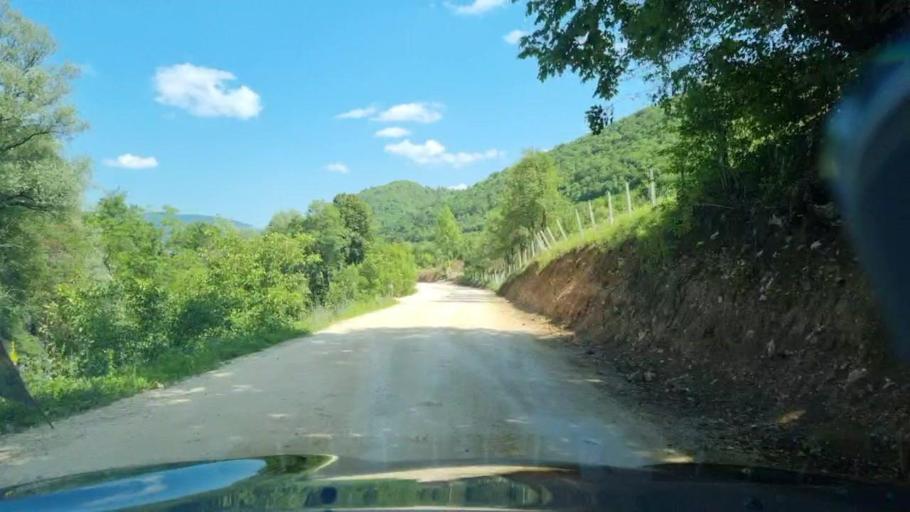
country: BA
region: Federation of Bosnia and Herzegovina
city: Kljuc
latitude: 44.5684
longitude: 16.8343
